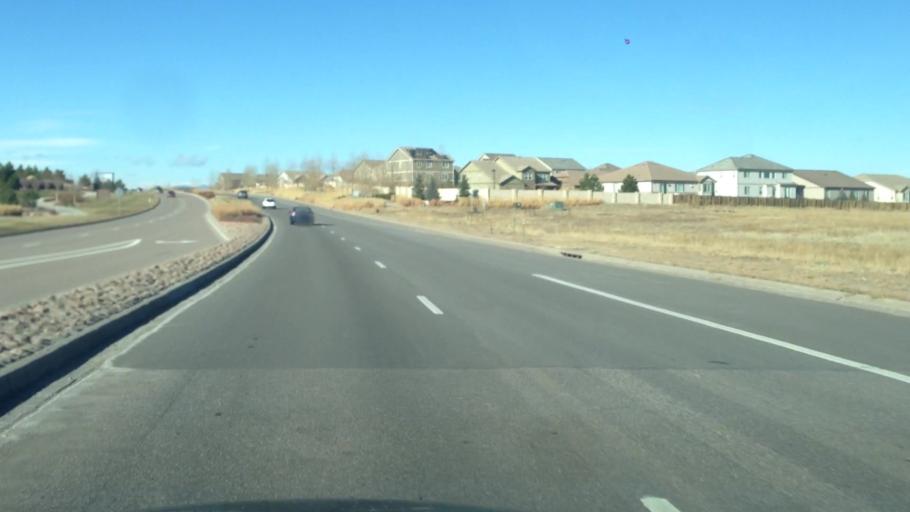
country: US
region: Colorado
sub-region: Douglas County
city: Stonegate
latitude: 39.5190
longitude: -104.8228
